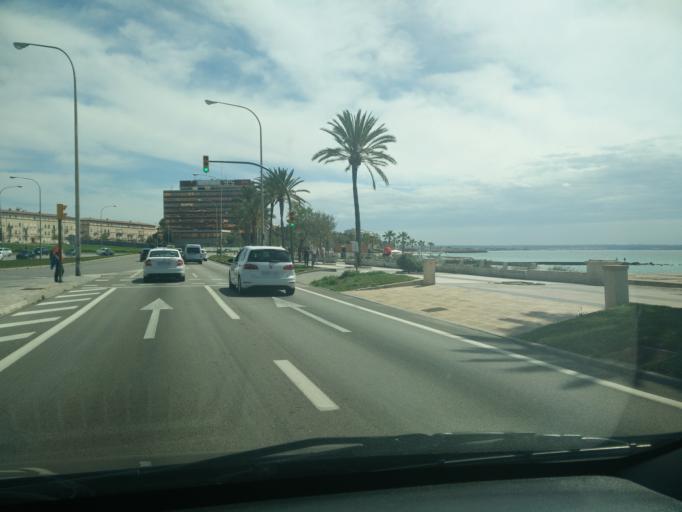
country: ES
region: Balearic Islands
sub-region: Illes Balears
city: Palma
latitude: 39.5643
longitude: 2.6561
